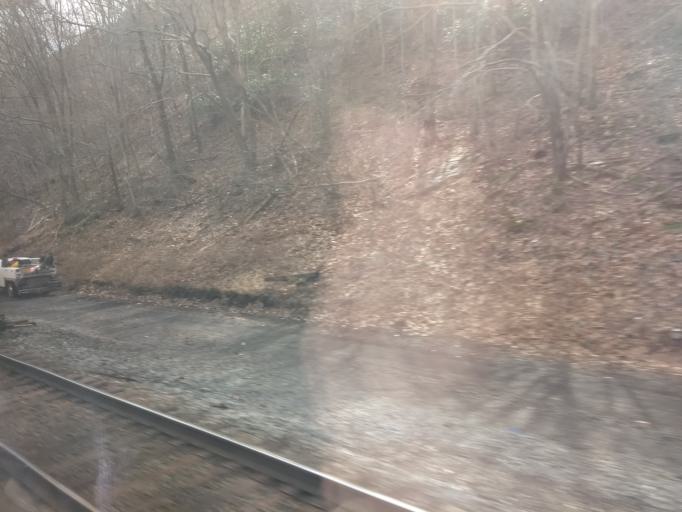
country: US
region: Pennsylvania
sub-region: Huntingdon County
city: Mount Union
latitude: 40.3892
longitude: -77.9009
